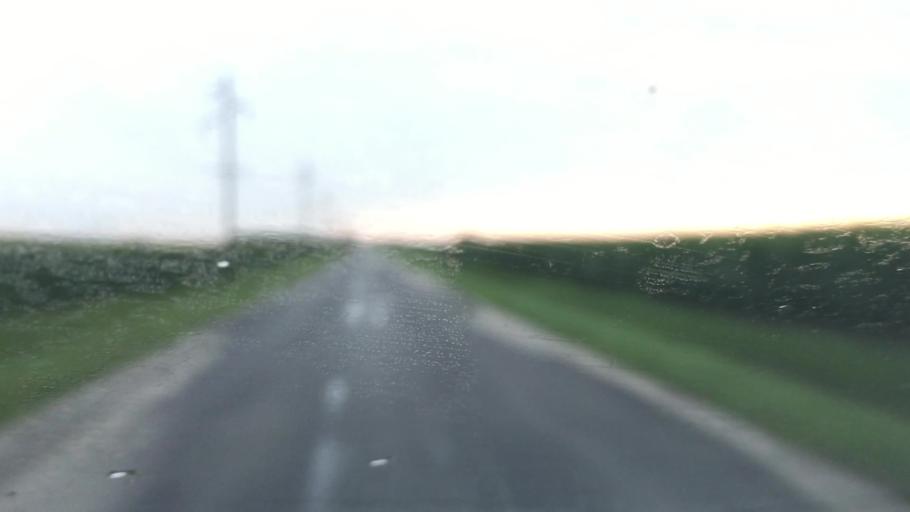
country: US
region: Iowa
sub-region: Lee County
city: Fort Madison
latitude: 40.5533
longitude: -91.2688
